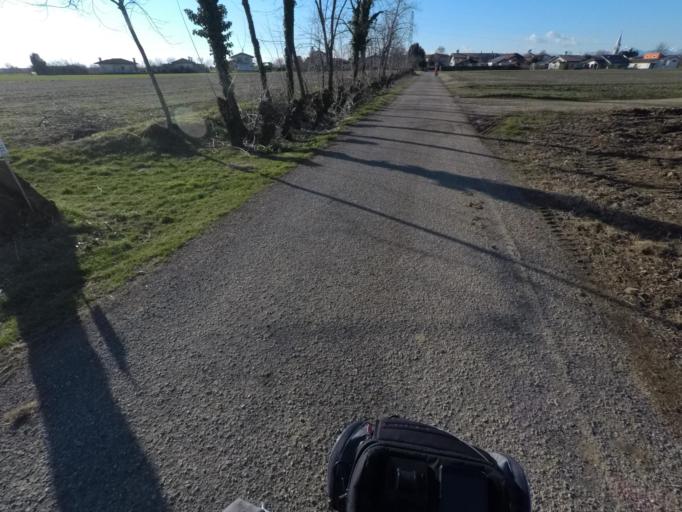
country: IT
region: Friuli Venezia Giulia
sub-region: Provincia di Udine
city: Remanzacco
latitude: 46.1013
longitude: 13.3135
